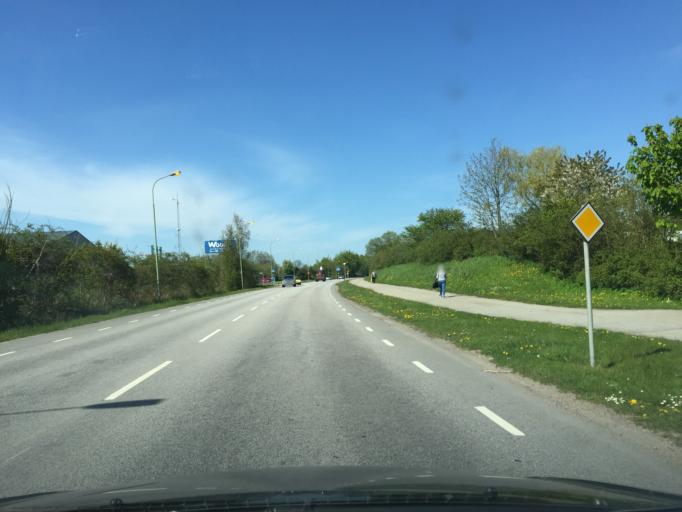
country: SE
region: Skane
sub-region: Skurups Kommun
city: Skurup
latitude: 55.4821
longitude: 13.5030
